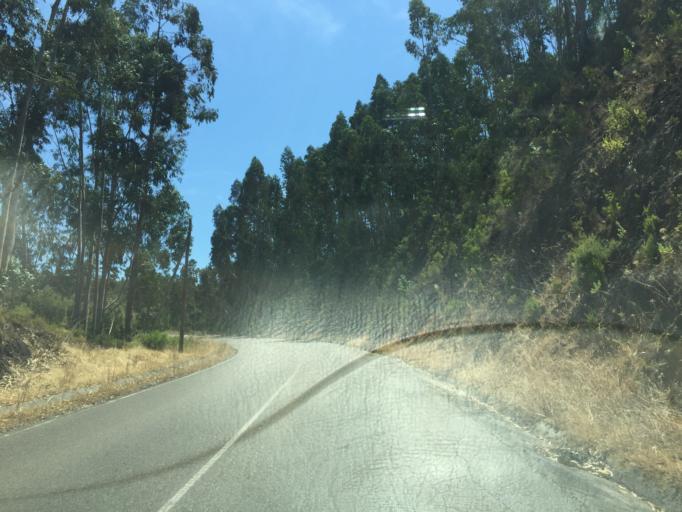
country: PT
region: Santarem
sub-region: Tomar
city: Tomar
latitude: 39.5922
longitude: -8.3442
